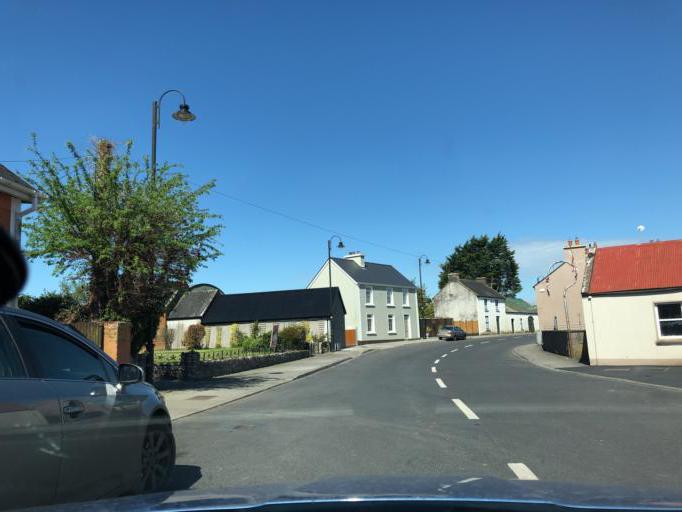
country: IE
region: Connaught
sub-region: County Galway
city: Portumna
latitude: 53.1499
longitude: -8.3735
